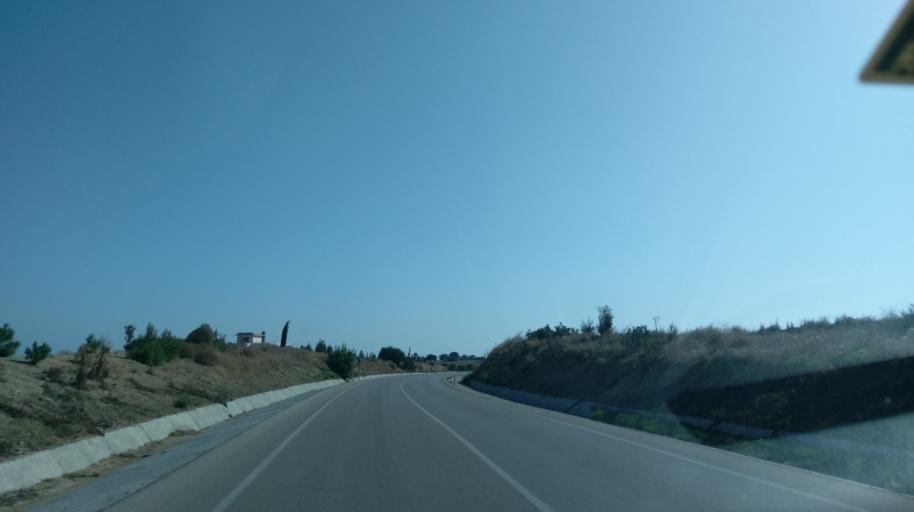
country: CY
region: Ammochostos
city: Leonarisso
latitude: 35.3920
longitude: 34.0080
